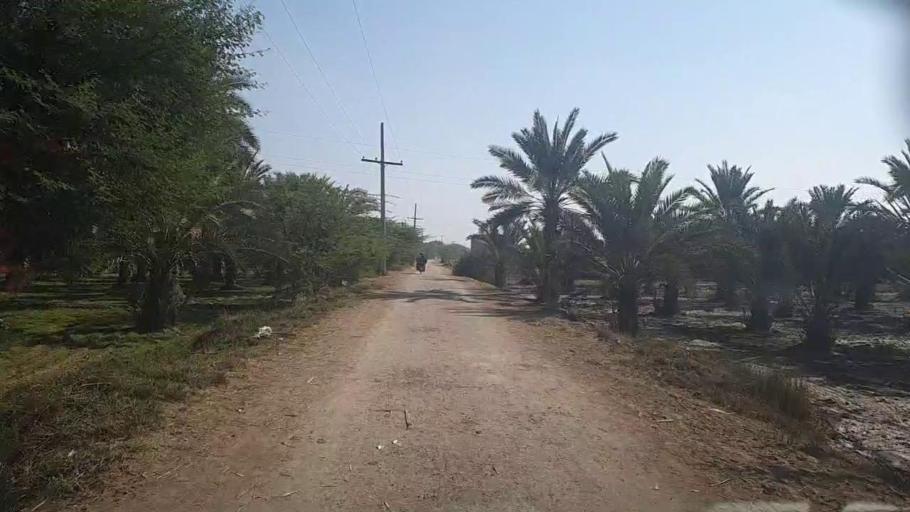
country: PK
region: Sindh
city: Kot Diji
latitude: 27.4381
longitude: 68.7107
